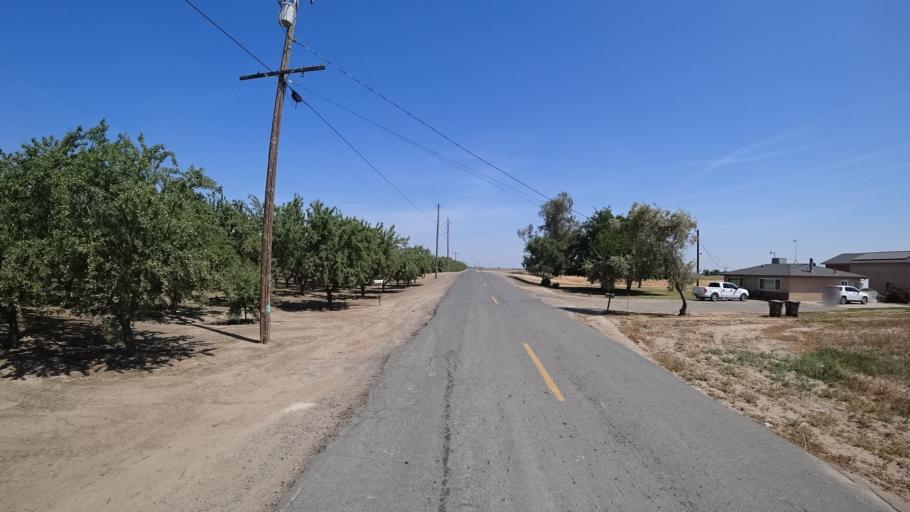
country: US
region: California
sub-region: Fresno County
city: Riverdale
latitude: 36.3978
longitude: -119.8691
